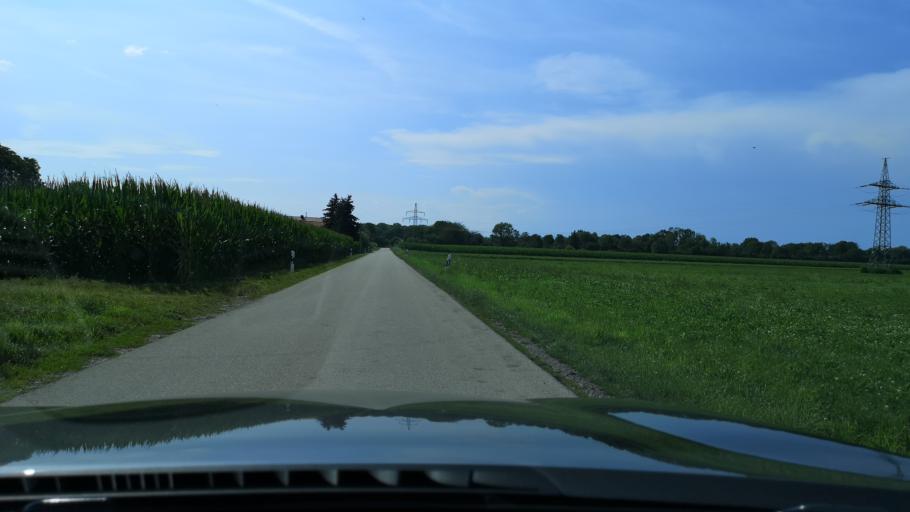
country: DE
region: Bavaria
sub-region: Upper Bavaria
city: Pliening
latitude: 48.2074
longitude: 11.7729
